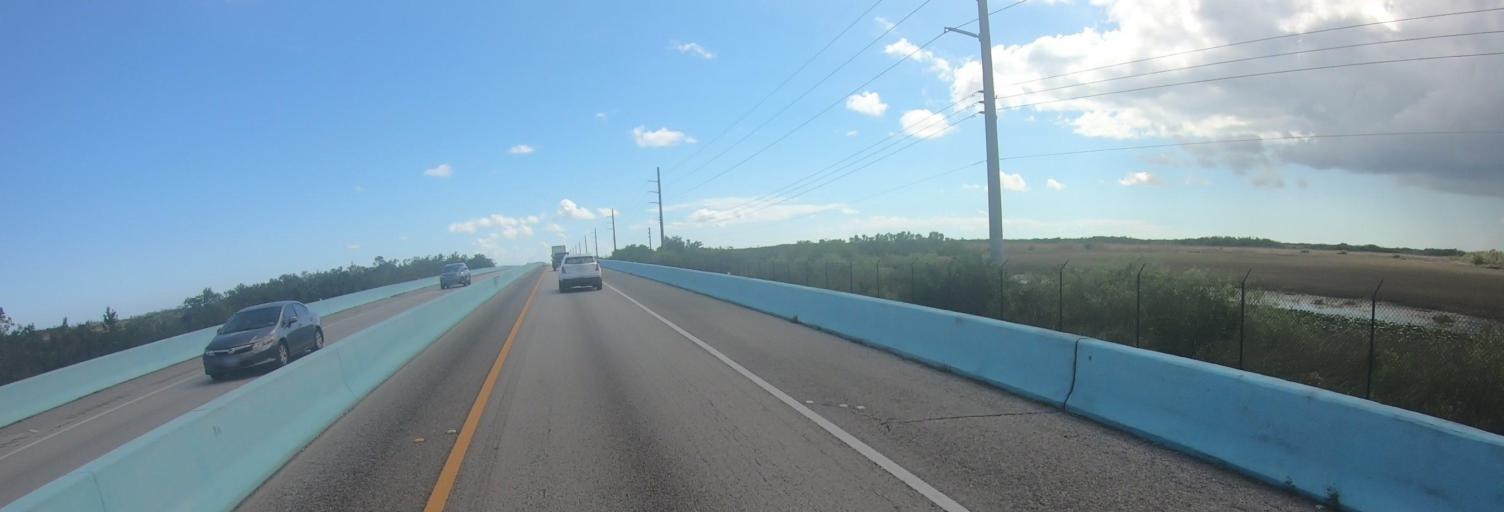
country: US
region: Florida
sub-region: Miami-Dade County
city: Florida City
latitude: 25.3330
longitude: -80.4543
